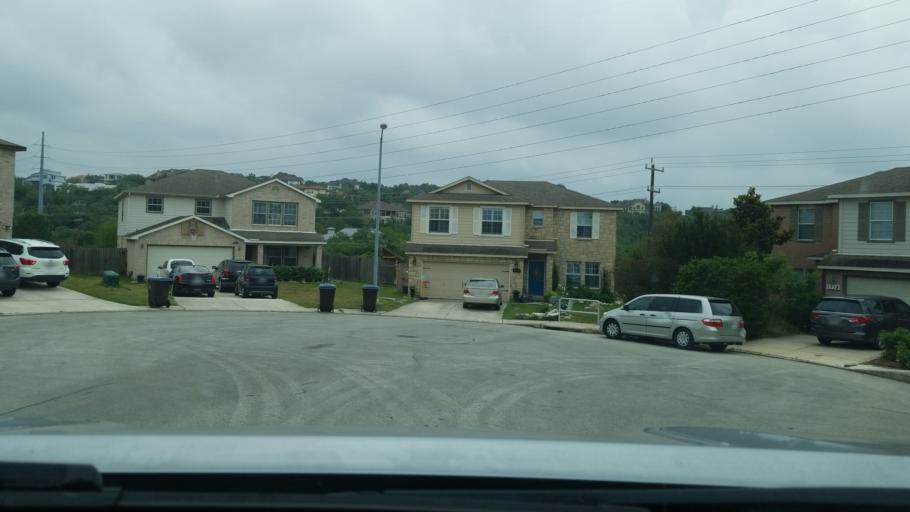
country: US
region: Texas
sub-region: Bexar County
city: Timberwood Park
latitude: 29.6803
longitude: -98.4646
